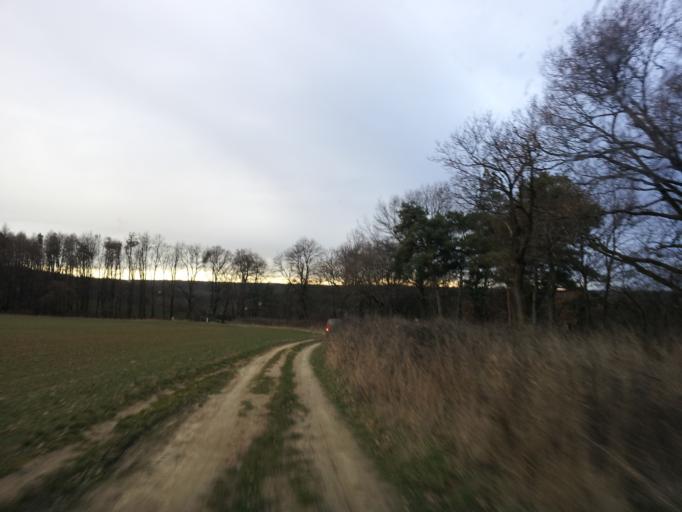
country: AT
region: Burgenland
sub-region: Politischer Bezirk Oberpullendorf
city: Lutzmannsburg
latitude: 47.3907
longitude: 16.6231
